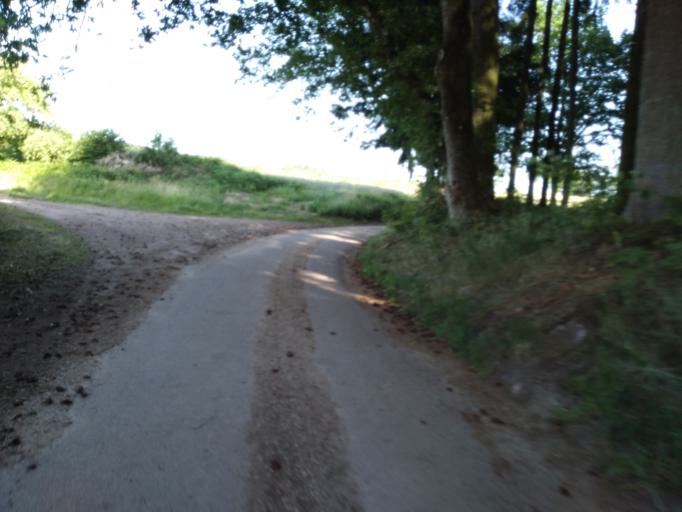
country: FR
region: Bourgogne
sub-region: Departement de la Cote-d'Or
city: Saulieu
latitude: 47.2842
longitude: 4.1471
